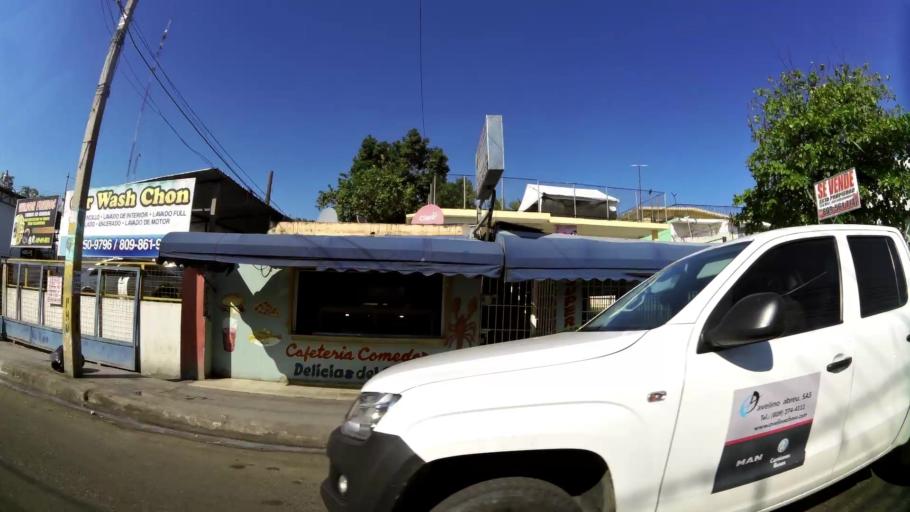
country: DO
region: Nacional
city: Santo Domingo
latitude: 18.4771
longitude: -69.9751
